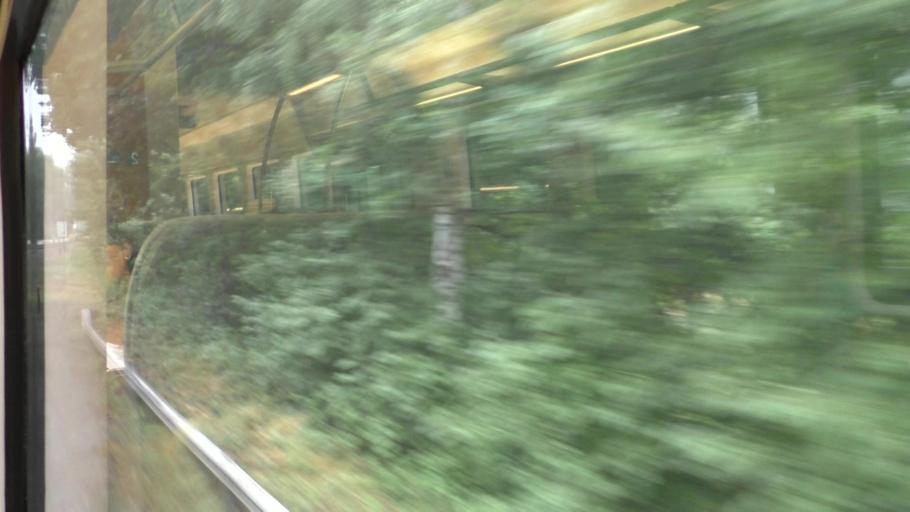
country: DE
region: Saxony
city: Demitz-Thumitz
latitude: 51.0987
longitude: 14.2354
